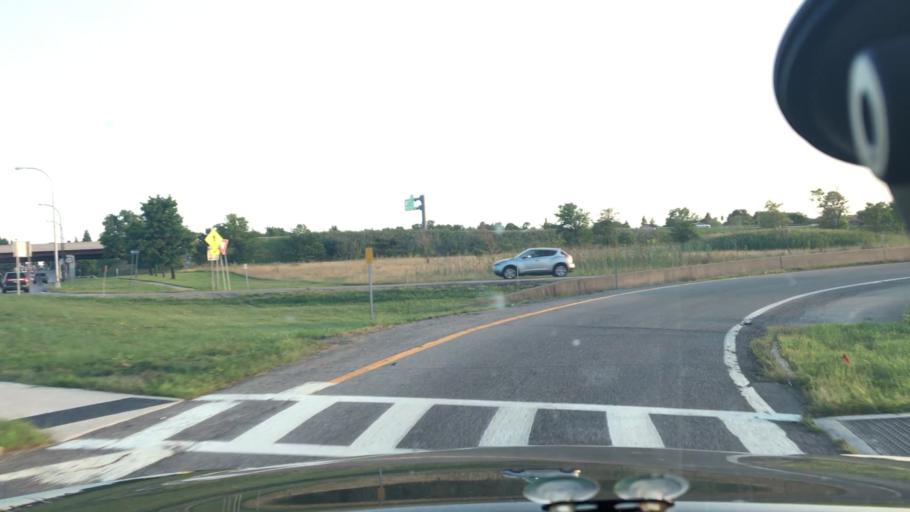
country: US
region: New York
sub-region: Erie County
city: Tonawanda
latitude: 42.9973
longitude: -78.8750
